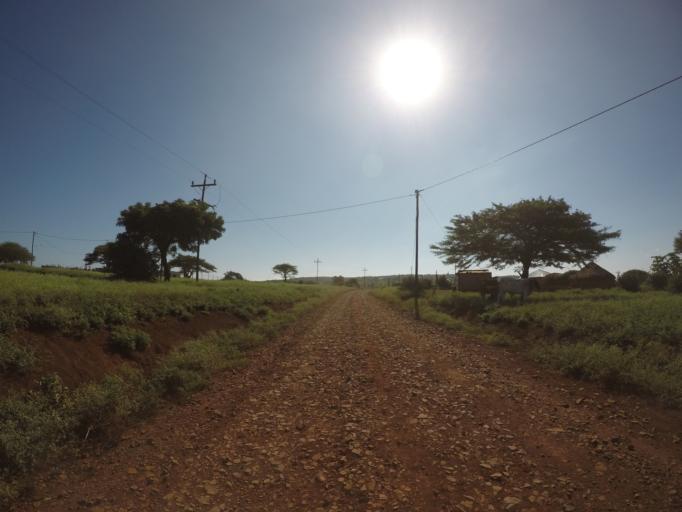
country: ZA
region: KwaZulu-Natal
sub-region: uThungulu District Municipality
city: Empangeni
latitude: -28.5724
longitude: 31.7272
